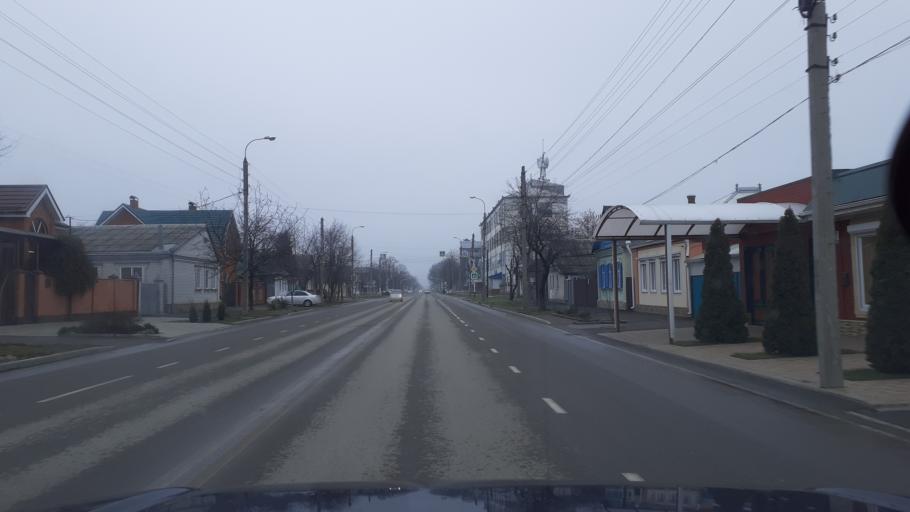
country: RU
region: Adygeya
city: Maykop
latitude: 44.6147
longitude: 40.0858
